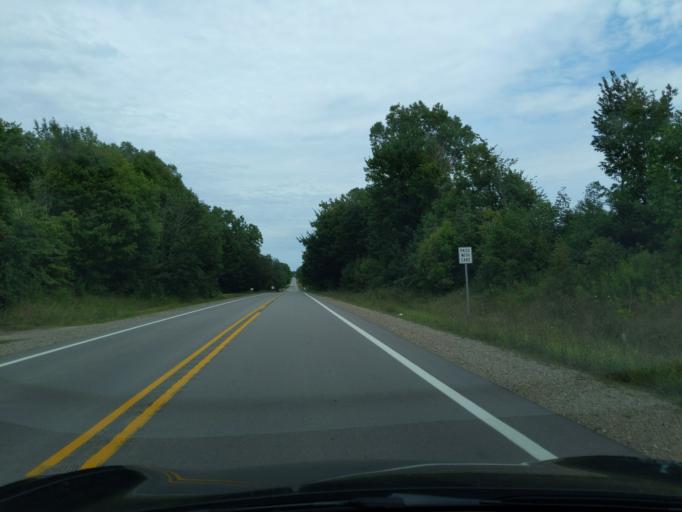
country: US
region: Michigan
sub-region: Barry County
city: Nashville
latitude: 42.5674
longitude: -85.0200
